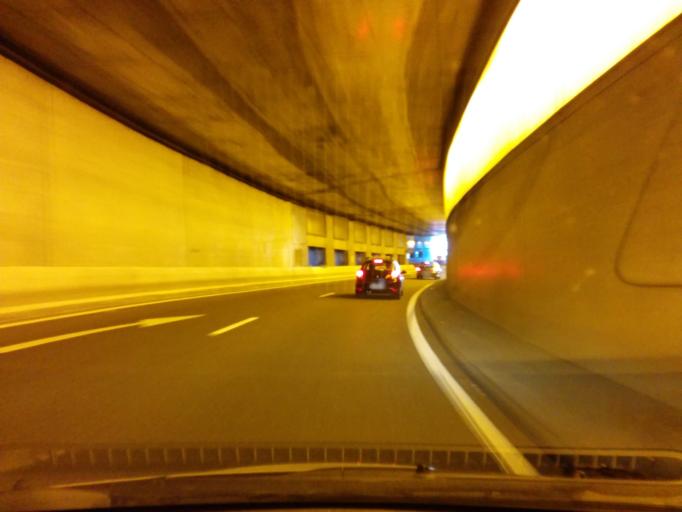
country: FR
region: Ile-de-France
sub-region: Departement des Hauts-de-Seine
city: Boulogne-Billancourt
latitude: 48.8484
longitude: 2.2518
